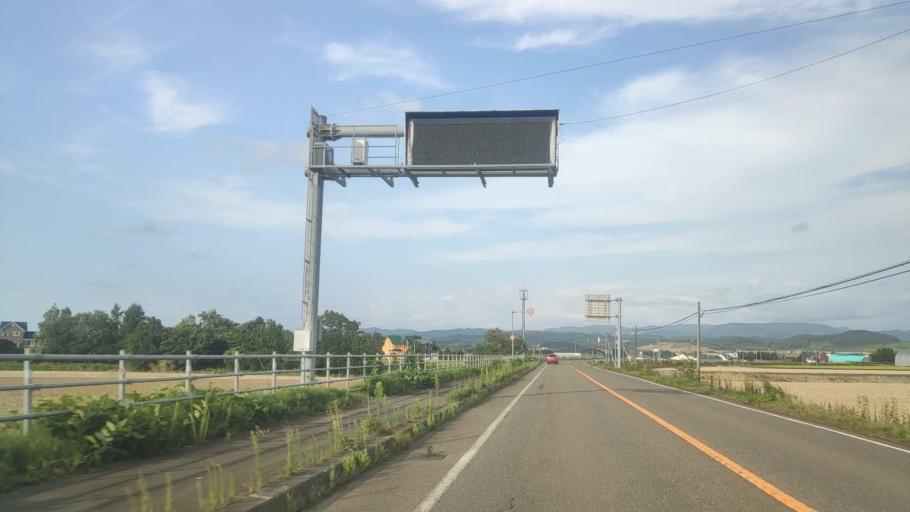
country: JP
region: Hokkaido
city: Iwamizawa
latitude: 43.0270
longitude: 141.8121
